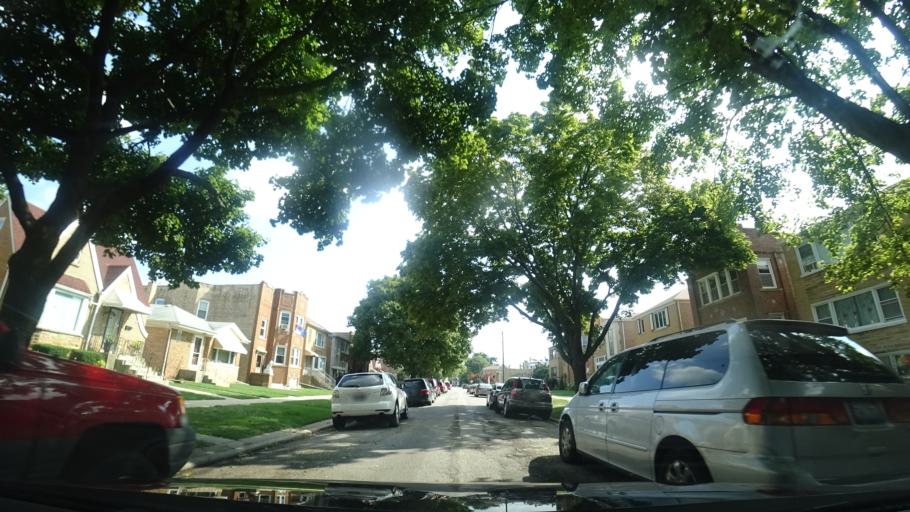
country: US
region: Illinois
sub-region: Cook County
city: Harwood Heights
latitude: 41.9729
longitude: -87.7722
